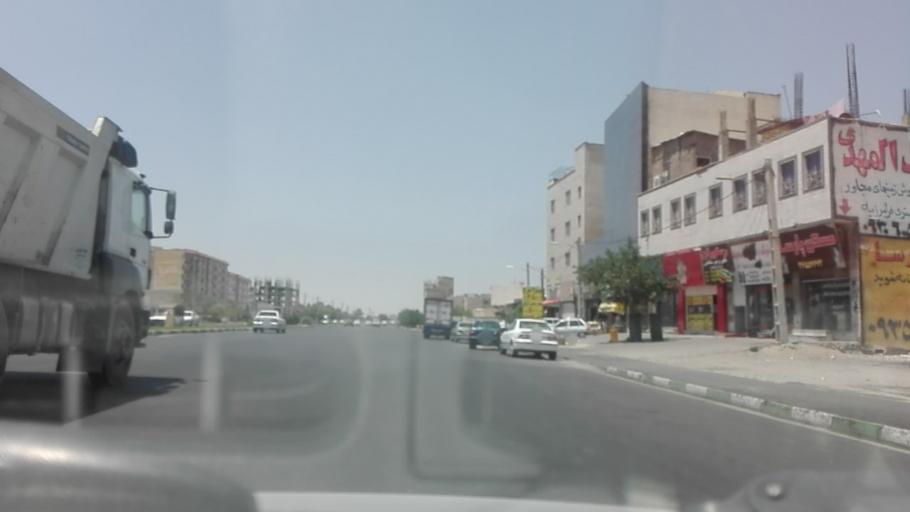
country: IR
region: Tehran
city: Malard
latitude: 35.7115
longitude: 50.9785
